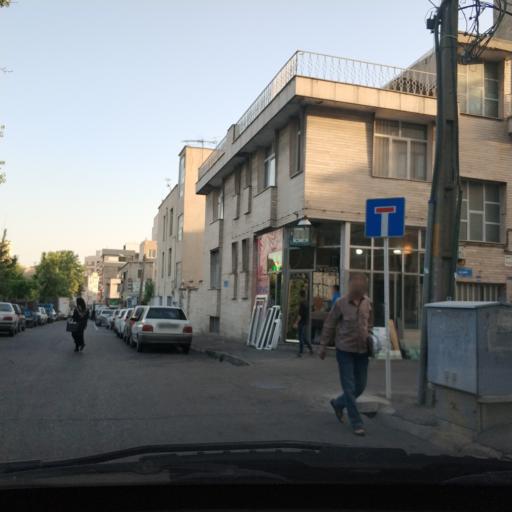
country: IR
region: Tehran
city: Tehran
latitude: 35.7185
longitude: 51.4772
